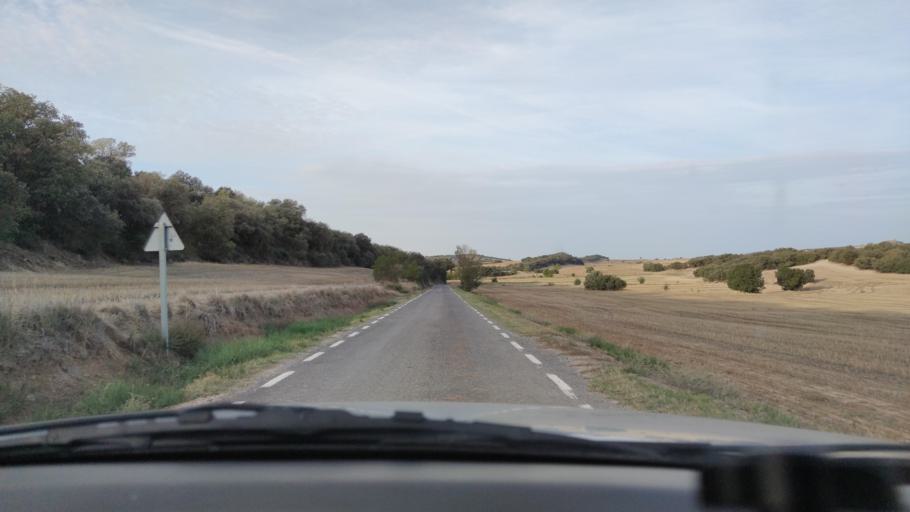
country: ES
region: Catalonia
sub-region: Provincia de Lleida
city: Agramunt
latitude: 41.8382
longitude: 1.0807
